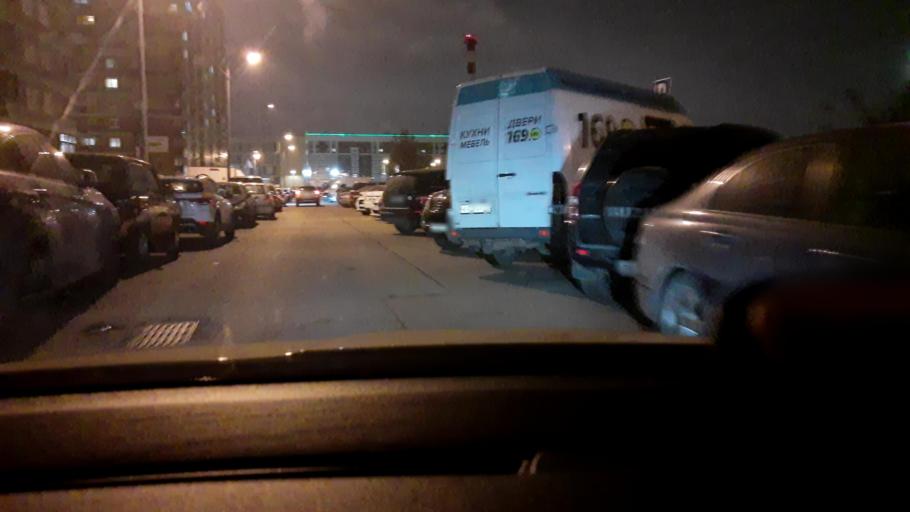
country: RU
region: Moscow
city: Khimki
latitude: 55.8702
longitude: 37.4030
